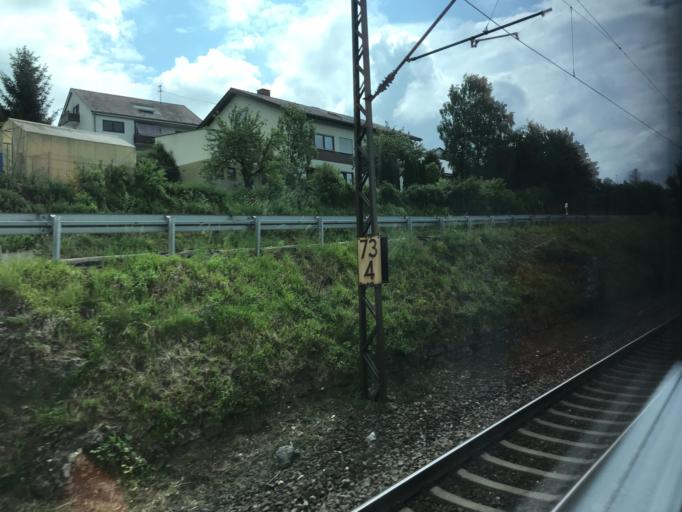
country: DE
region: Baden-Wuerttemberg
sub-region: Tuebingen Region
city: Lonsee
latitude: 48.5411
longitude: 9.9212
